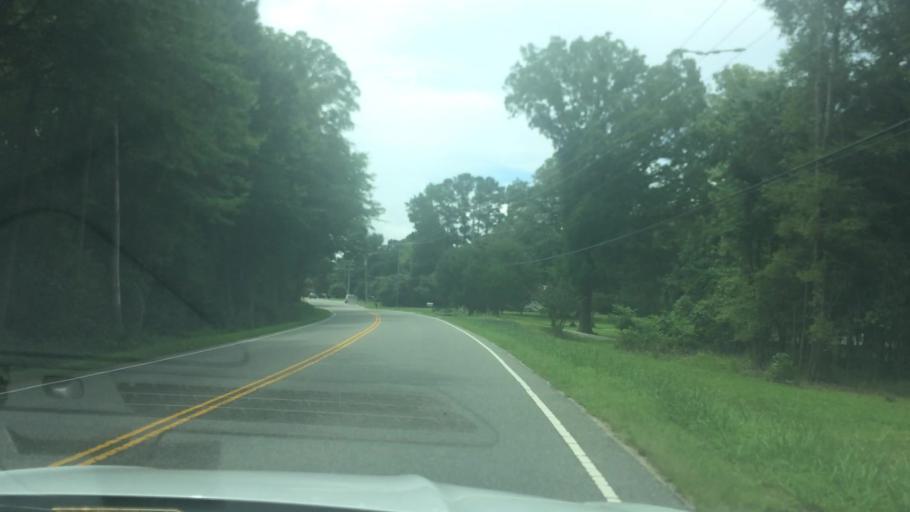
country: US
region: Virginia
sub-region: James City County
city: Williamsburg
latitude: 37.2579
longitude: -76.7650
